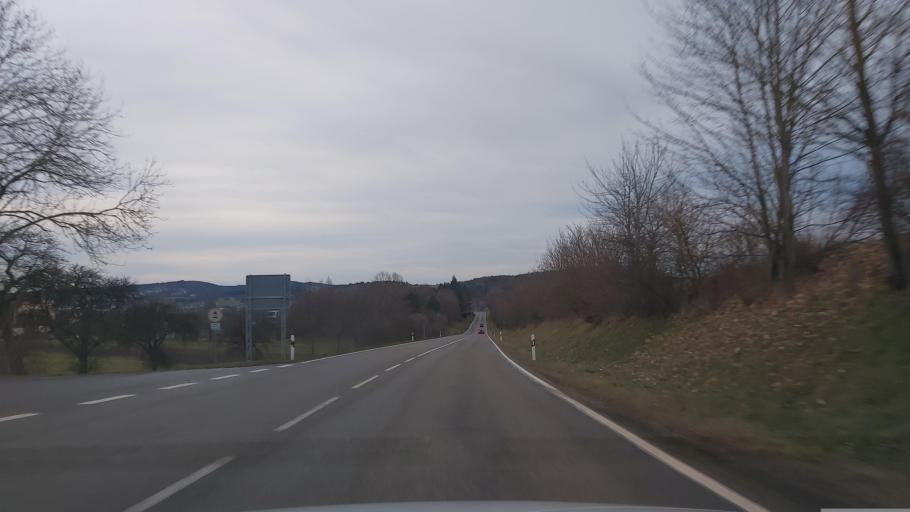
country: DE
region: Baden-Wuerttemberg
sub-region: Tuebingen Region
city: Munsingen
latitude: 48.4051
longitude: 9.5064
